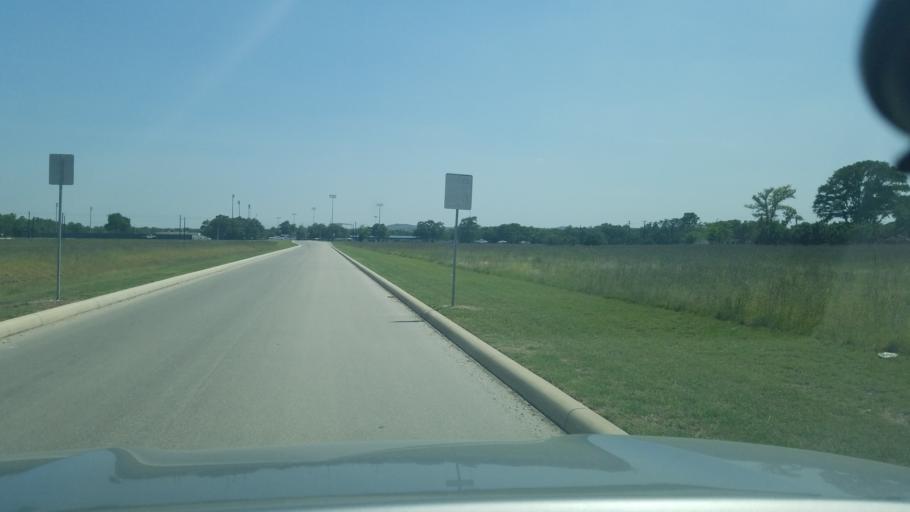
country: US
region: Texas
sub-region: Kendall County
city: Boerne
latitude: 29.7909
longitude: -98.7015
